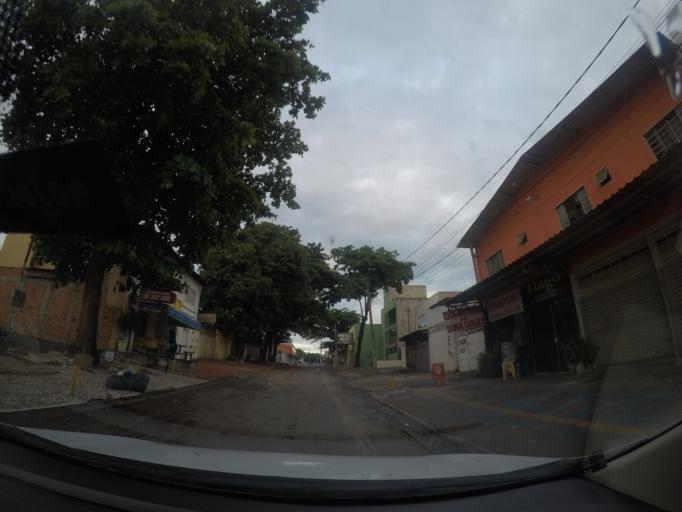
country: BR
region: Goias
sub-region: Goiania
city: Goiania
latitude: -16.6575
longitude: -49.2565
